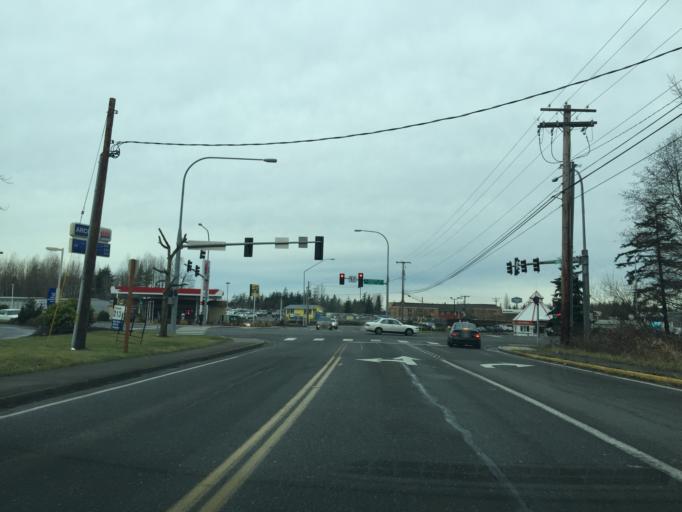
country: US
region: Washington
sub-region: Whatcom County
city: Marietta-Alderwood
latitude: 48.7857
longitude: -122.5189
